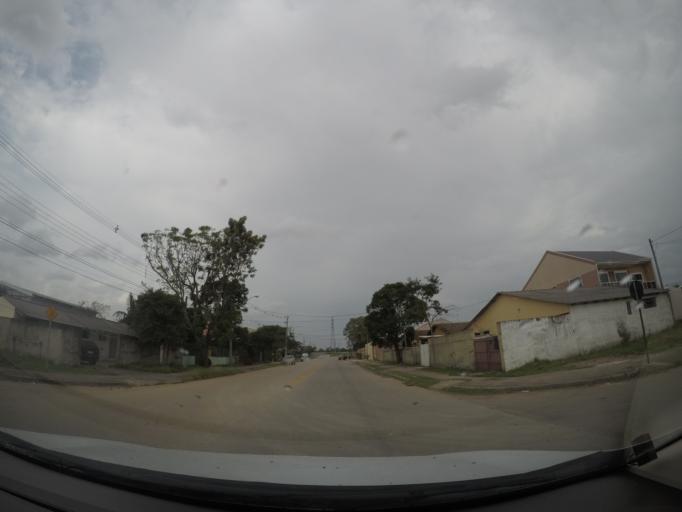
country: BR
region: Parana
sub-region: Sao Jose Dos Pinhais
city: Sao Jose dos Pinhais
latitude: -25.5033
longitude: -49.2140
